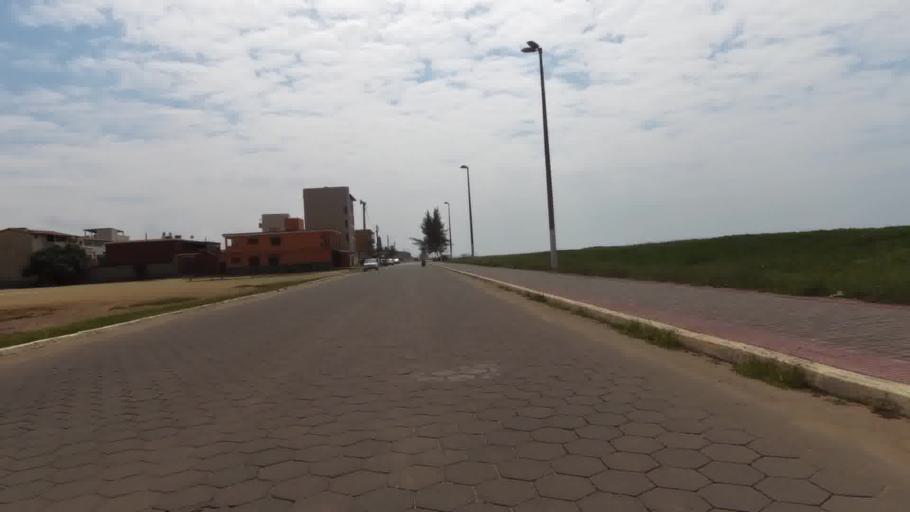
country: BR
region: Espirito Santo
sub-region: Marataizes
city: Marataizes
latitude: -21.0231
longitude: -40.8113
